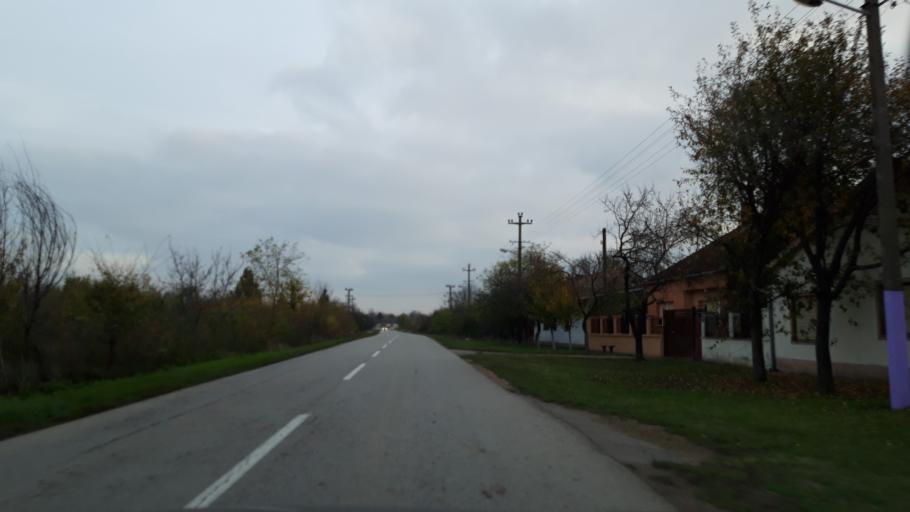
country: RS
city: Sanad
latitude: 45.9847
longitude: 20.1109
